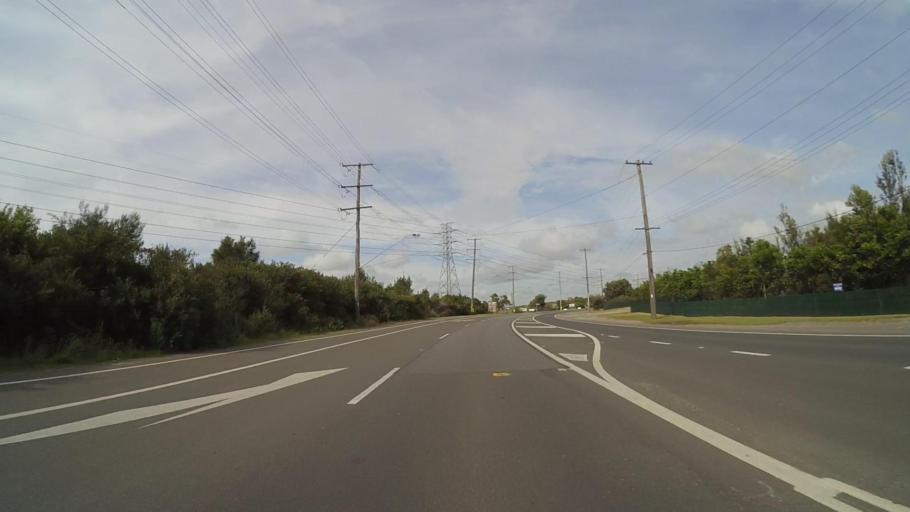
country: AU
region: New South Wales
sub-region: Sutherland Shire
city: Kurnell
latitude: -34.0236
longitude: 151.1907
